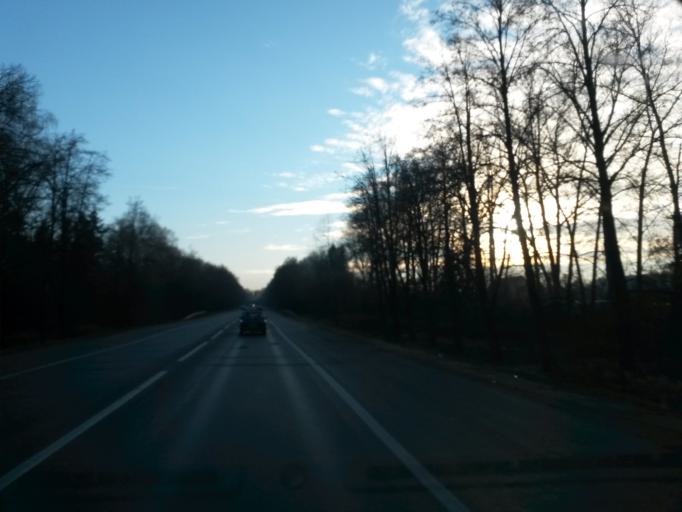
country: RU
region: Moskovskaya
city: Stolbovaya
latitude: 55.2546
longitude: 37.5070
